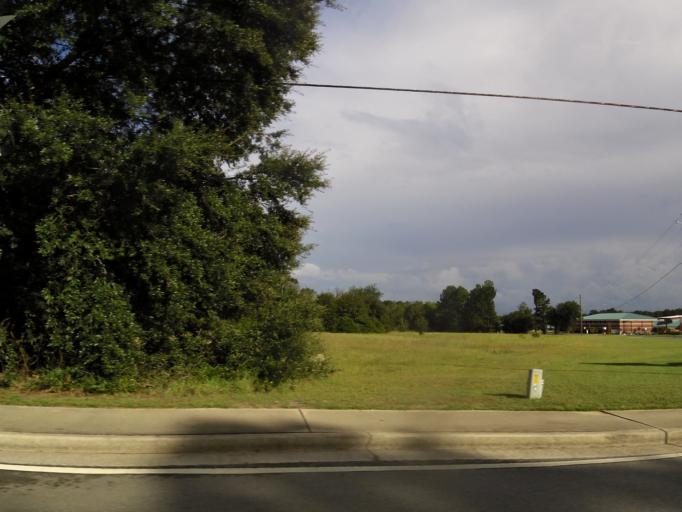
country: US
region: Georgia
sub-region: Liberty County
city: Hinesville
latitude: 31.8161
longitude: -81.6012
